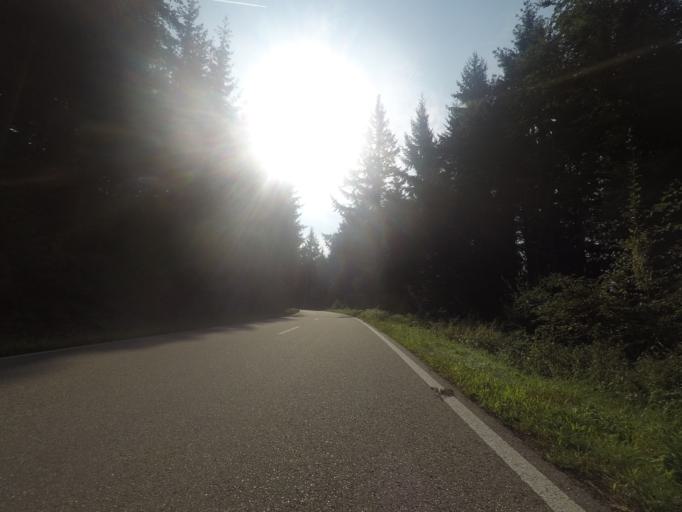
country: DE
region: Baden-Wuerttemberg
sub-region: Karlsruhe Region
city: Malsch
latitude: 48.8528
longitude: 8.3517
